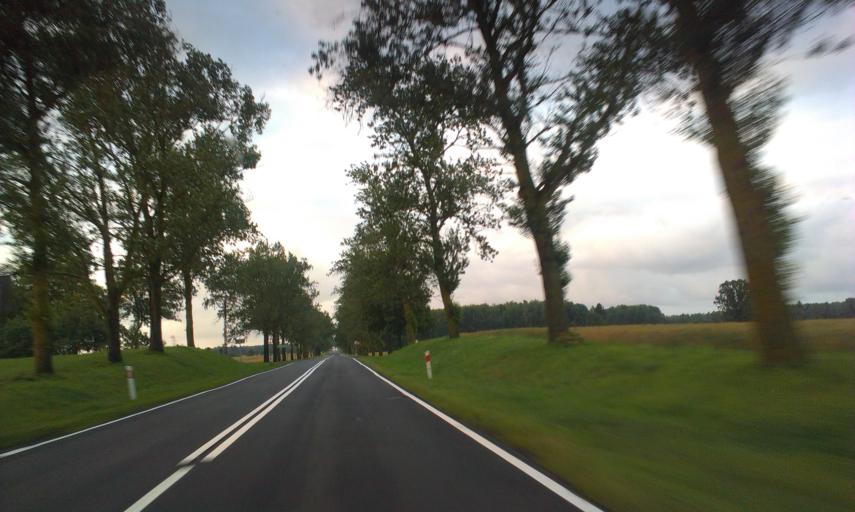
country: PL
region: Greater Poland Voivodeship
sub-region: Powiat zlotowski
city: Okonek
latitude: 53.5924
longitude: 16.8162
